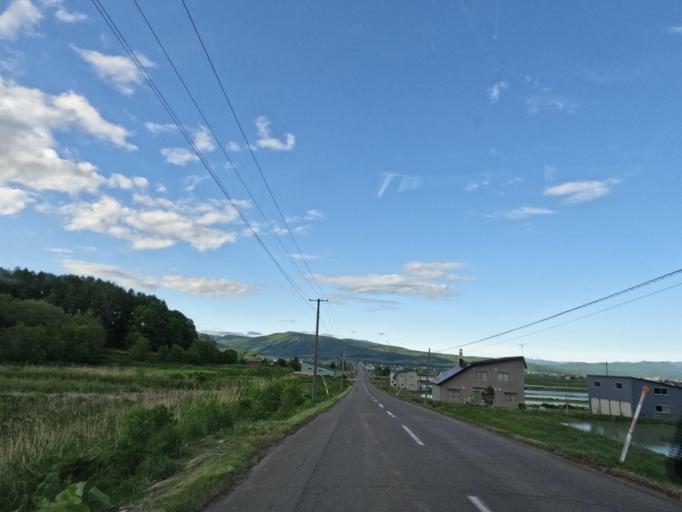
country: JP
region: Hokkaido
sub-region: Asahikawa-shi
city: Asahikawa
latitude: 43.8837
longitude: 142.4576
